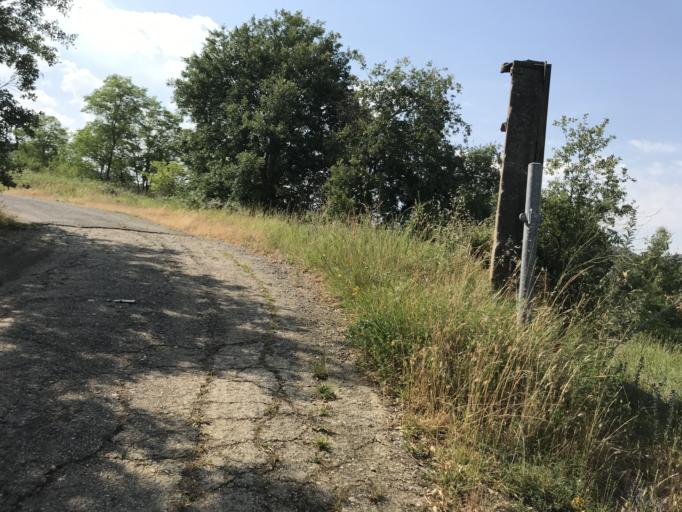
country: ES
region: Basque Country
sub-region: Provincia de Alava
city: Gasteiz / Vitoria
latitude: 42.8161
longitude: -2.6454
